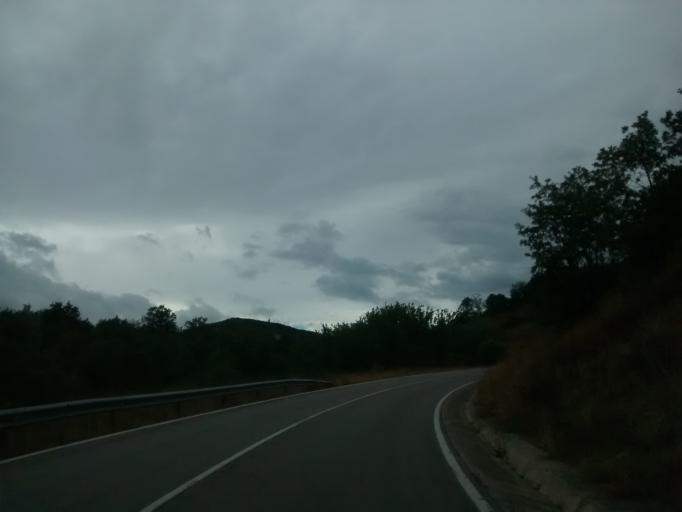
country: ES
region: Castille and Leon
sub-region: Provincia de Palencia
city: Berzosilla
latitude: 42.8593
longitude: -4.0438
